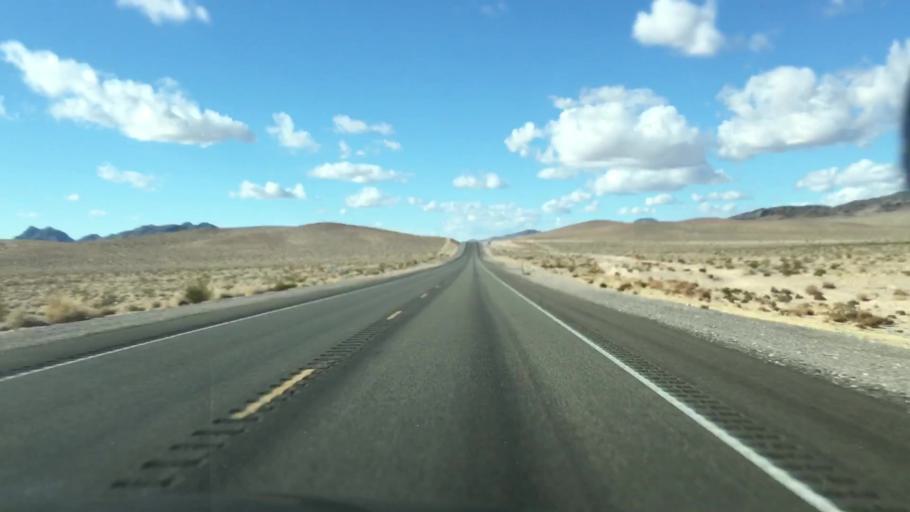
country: US
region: Nevada
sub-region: Nye County
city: Pahrump
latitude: 36.6075
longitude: -116.2636
